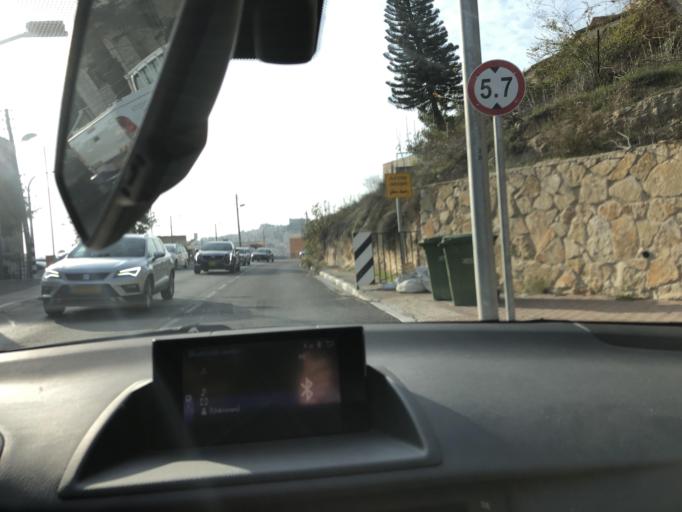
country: IL
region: Northern District
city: Nazareth
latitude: 32.7089
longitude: 35.3079
